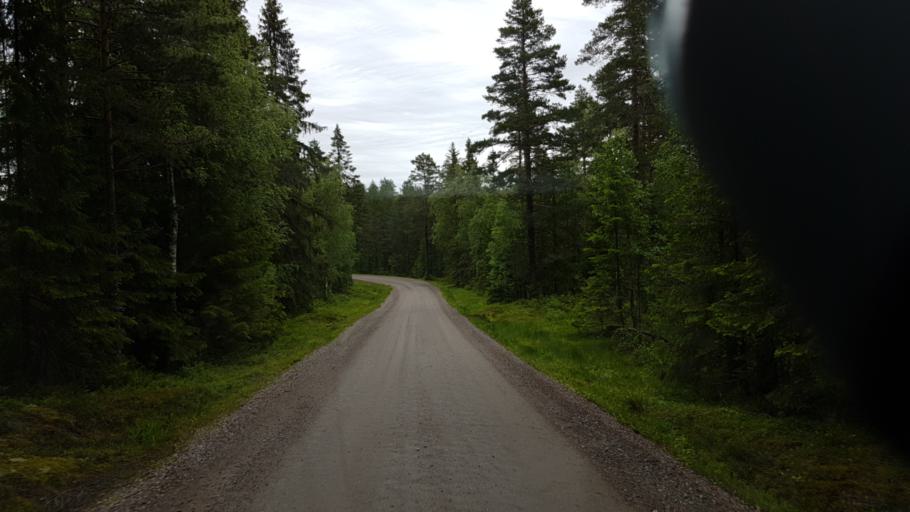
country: NO
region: Ostfold
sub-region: Romskog
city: Romskog
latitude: 59.7124
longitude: 12.0139
